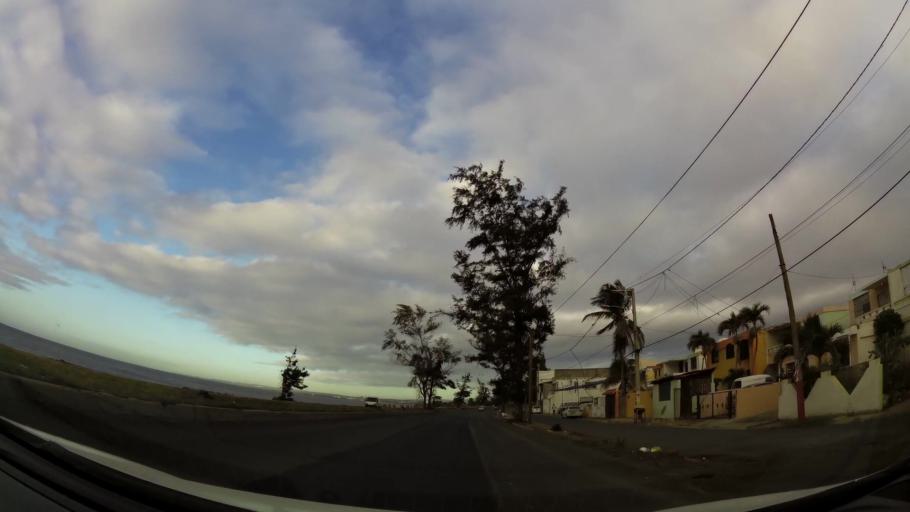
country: DO
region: Nacional
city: Bella Vista
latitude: 18.4270
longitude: -69.9718
